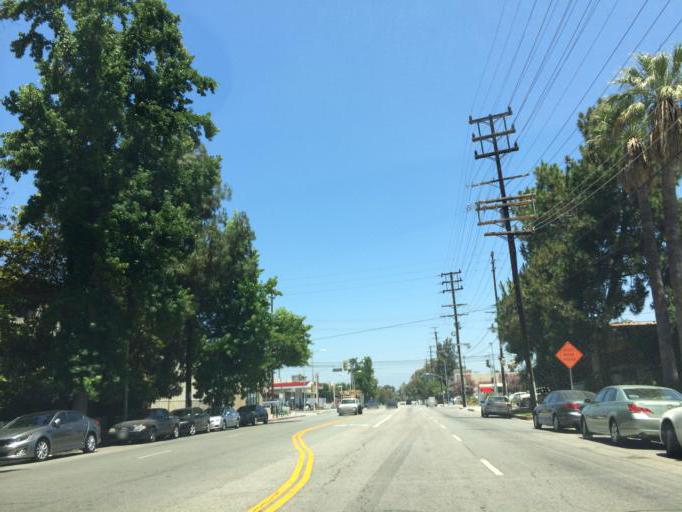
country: US
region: California
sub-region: Los Angeles County
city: North Hollywood
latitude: 34.1640
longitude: -118.4137
